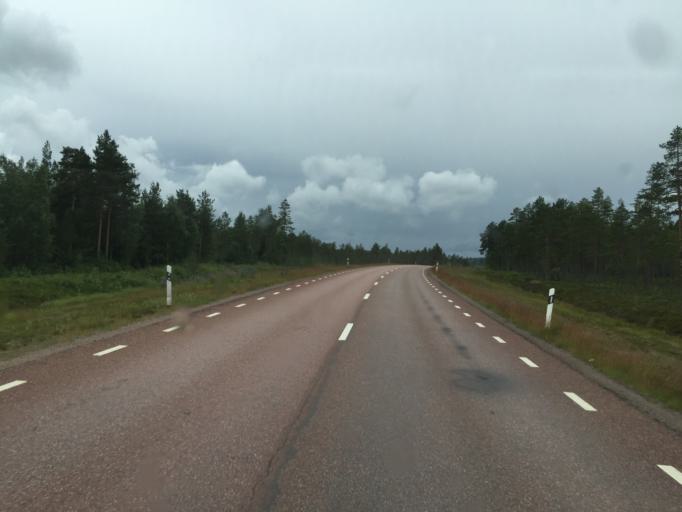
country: SE
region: Dalarna
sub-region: Malung-Saelens kommun
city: Malung
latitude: 60.6594
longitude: 13.6963
